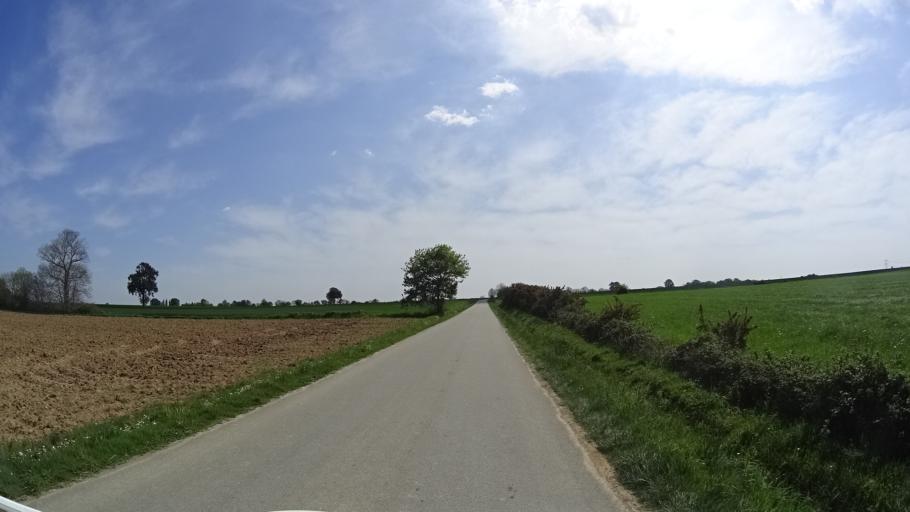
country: FR
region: Brittany
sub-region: Departement d'Ille-et-Vilaine
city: Torce
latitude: 48.0411
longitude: -1.2868
